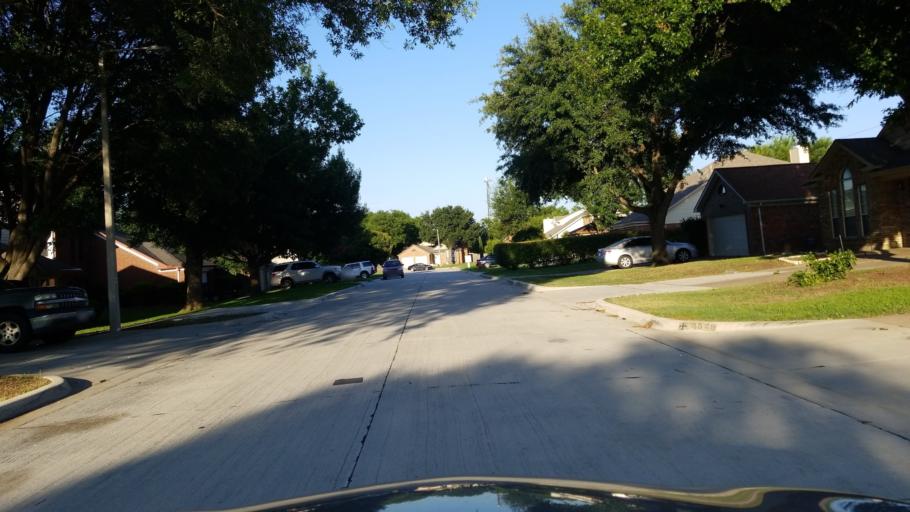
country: US
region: Texas
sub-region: Dallas County
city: Grand Prairie
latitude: 32.6918
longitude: -97.0384
